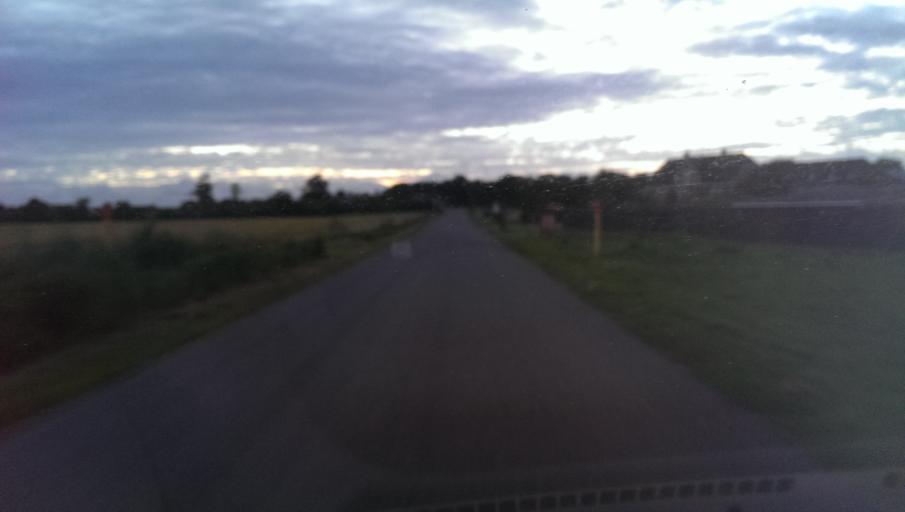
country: DK
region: South Denmark
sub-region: Esbjerg Kommune
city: Esbjerg
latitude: 55.5310
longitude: 8.4866
